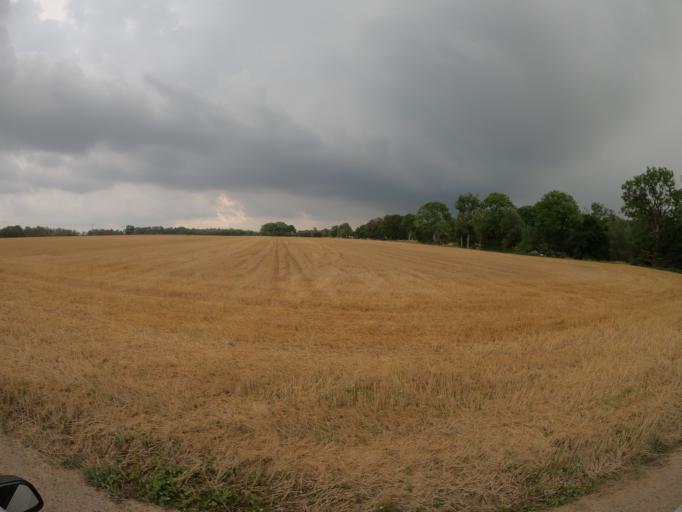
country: SE
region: Skane
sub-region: Lunds Kommun
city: Genarp
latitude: 55.6905
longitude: 13.3146
